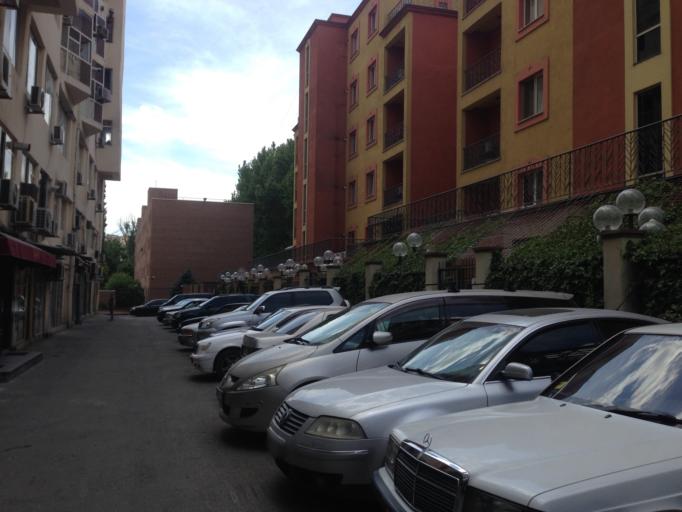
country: AM
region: Yerevan
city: Yerevan
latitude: 40.1736
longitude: 44.5098
